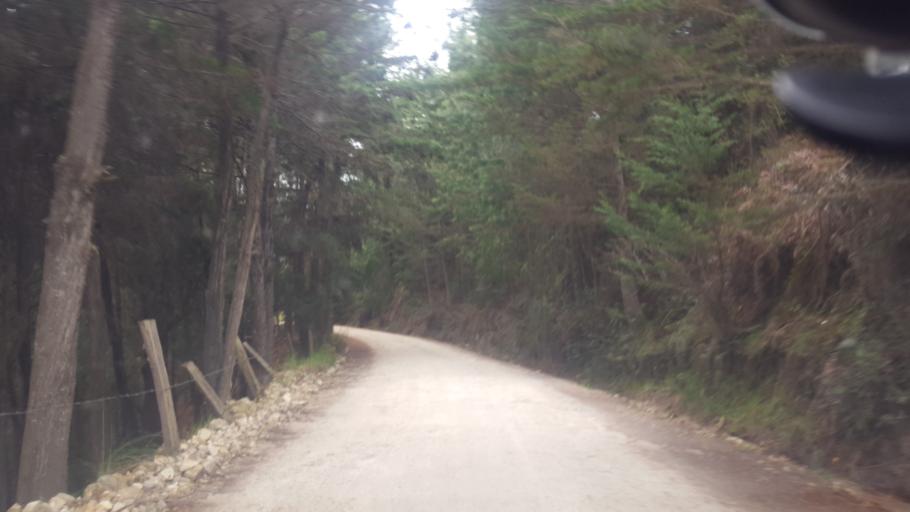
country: CO
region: Boyaca
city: Belen
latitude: 6.0041
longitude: -72.8469
